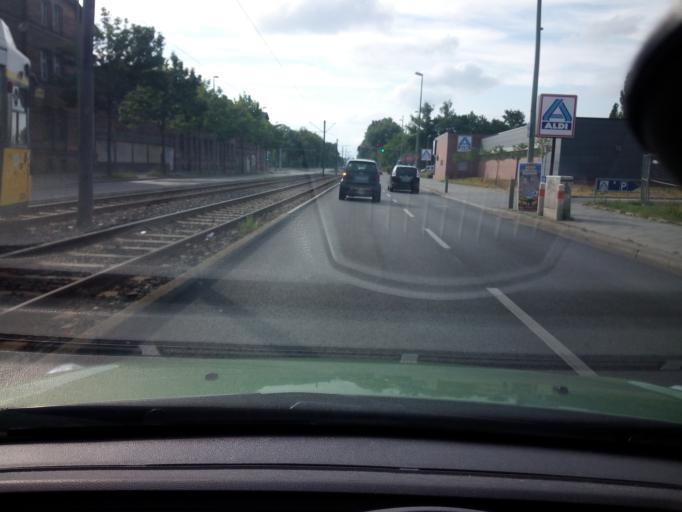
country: DE
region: Berlin
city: Rummelsburg
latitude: 52.4960
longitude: 13.4877
